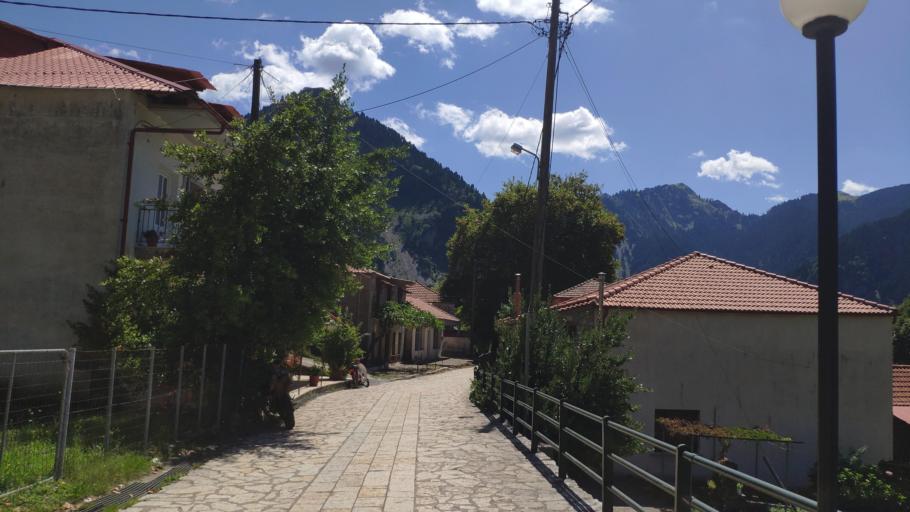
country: GR
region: Central Greece
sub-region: Nomos Evrytanias
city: Kerasochori
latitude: 39.1379
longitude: 21.6490
